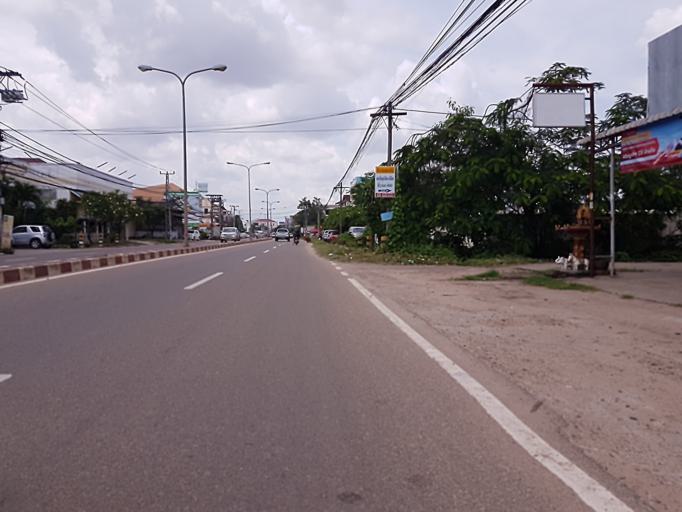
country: TH
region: Nong Khai
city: Si Chiang Mai
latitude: 17.9162
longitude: 102.6198
